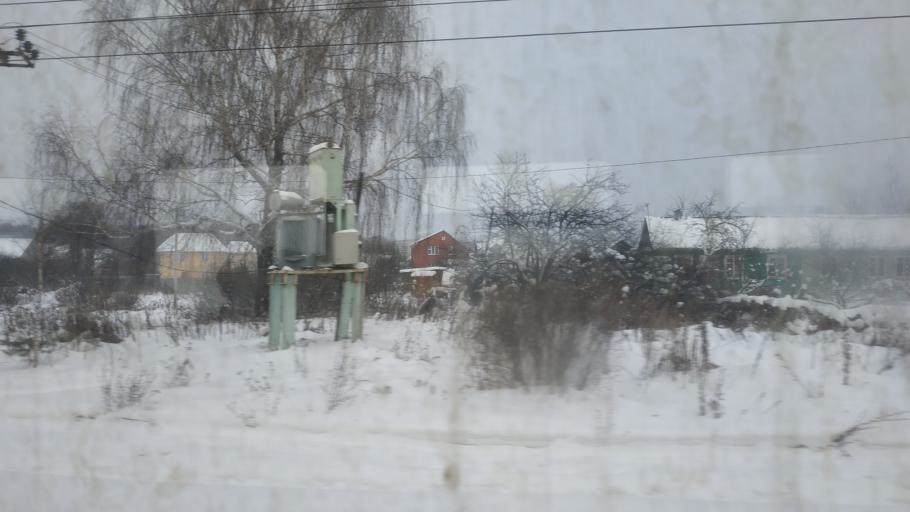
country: RU
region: Moskovskaya
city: Malyshevo
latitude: 55.5369
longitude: 38.3034
